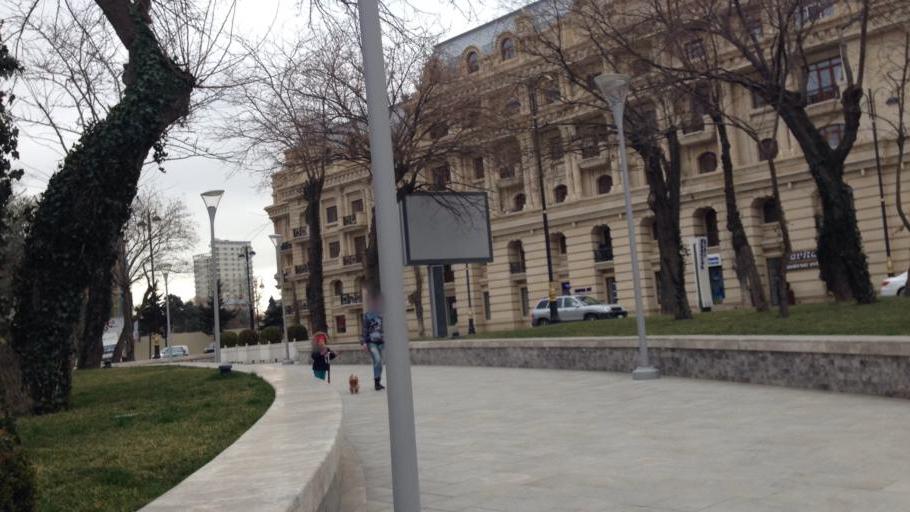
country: AZ
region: Baki
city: Baku
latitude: 40.3920
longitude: 49.8460
